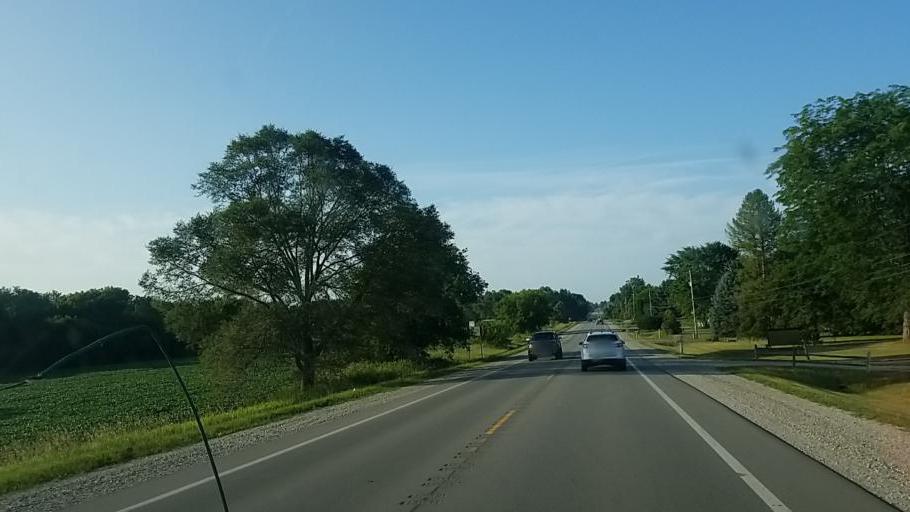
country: US
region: Michigan
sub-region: Montcalm County
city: Stanton
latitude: 43.2344
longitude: -85.0735
